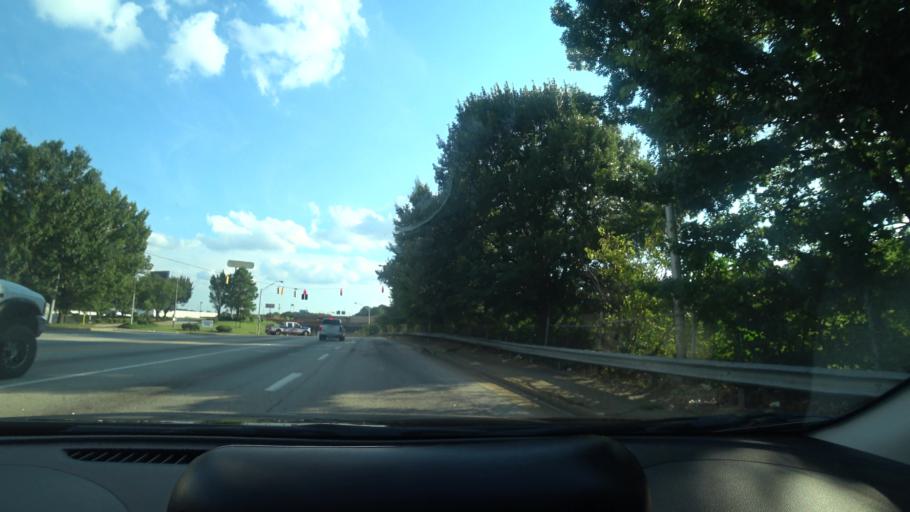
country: US
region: Georgia
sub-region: Fulton County
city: Atlanta
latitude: 33.7277
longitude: -84.3927
